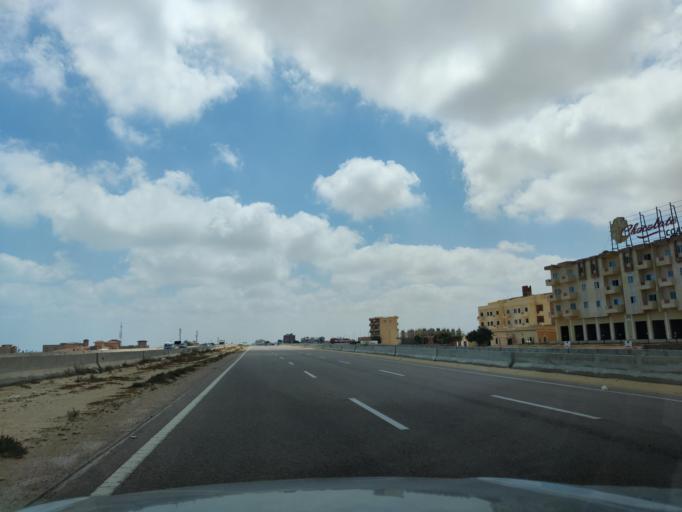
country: EG
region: Muhafazat Matruh
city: Al `Alamayn
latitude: 30.8193
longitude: 29.1602
